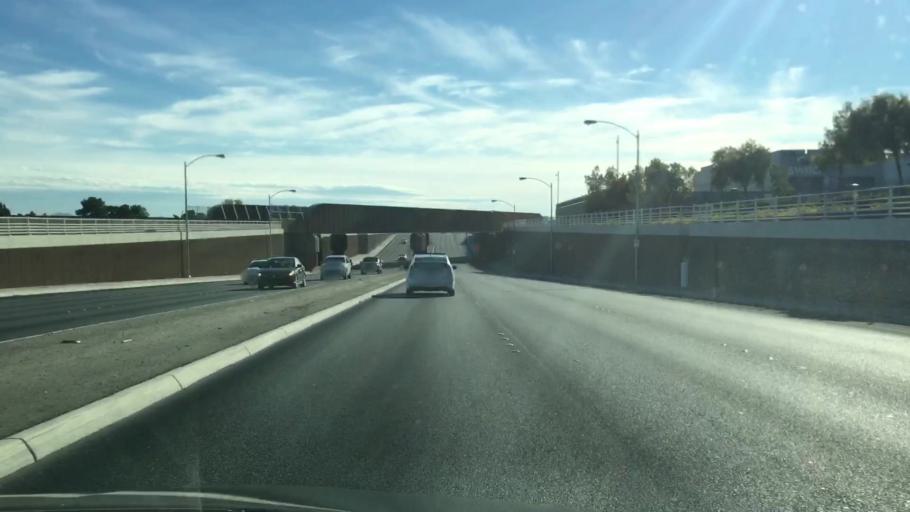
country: US
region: Nevada
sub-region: Clark County
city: Enterprise
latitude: 36.0615
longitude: -115.2079
